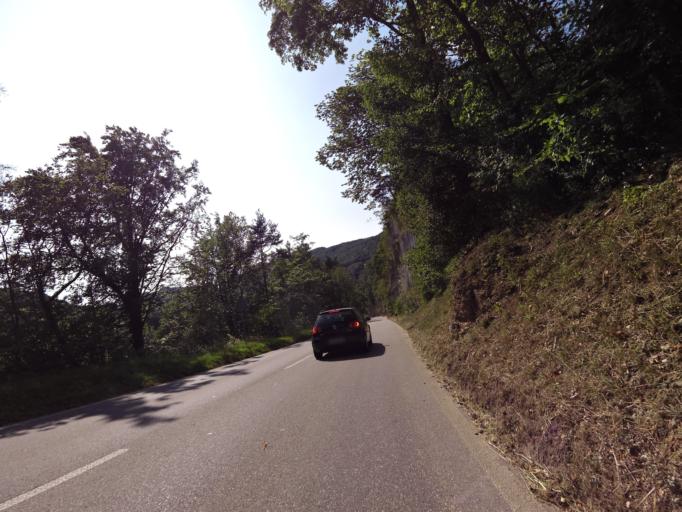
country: CH
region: Solothurn
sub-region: Bezirk Goesgen
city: Trimbach
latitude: 47.3726
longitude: 7.8697
